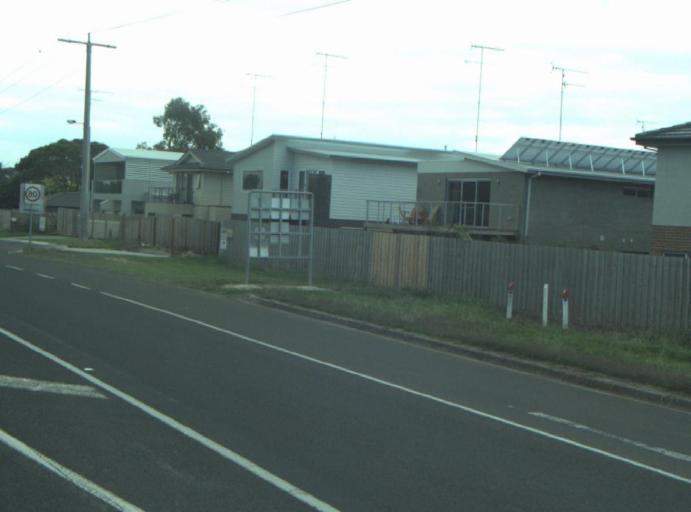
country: AU
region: Victoria
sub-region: Greater Geelong
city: Leopold
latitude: -38.2583
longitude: 144.5067
